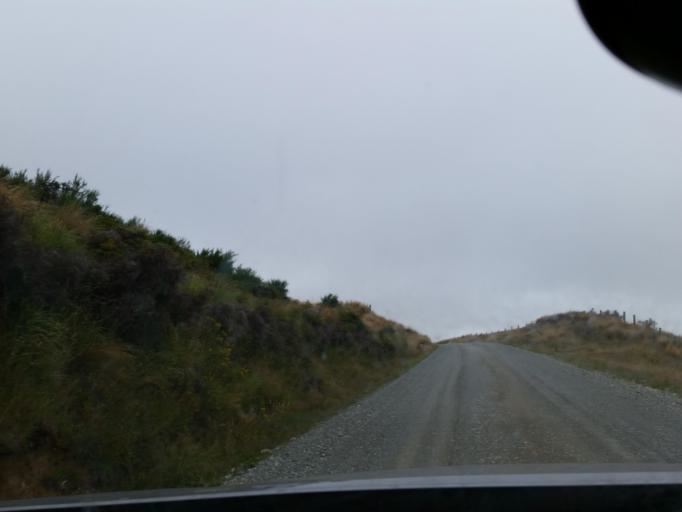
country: NZ
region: Southland
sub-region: Southland District
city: Te Anau
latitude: -45.4804
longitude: 168.1017
